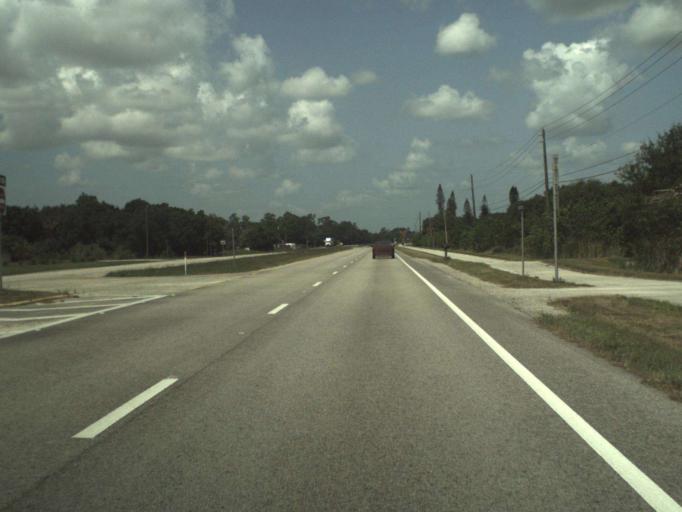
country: US
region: Florida
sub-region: Saint Lucie County
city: Fort Pierce South
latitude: 27.4049
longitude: -80.4364
